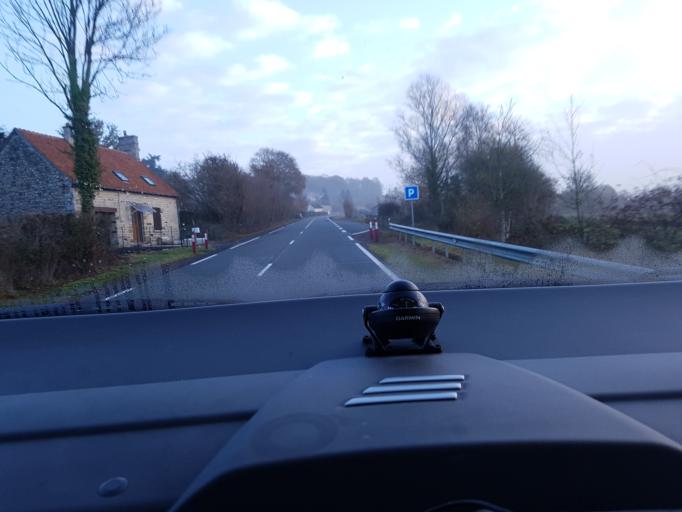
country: FR
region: Lower Normandy
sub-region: Departement de l'Orne
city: Domfront
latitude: 48.6059
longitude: -0.6029
